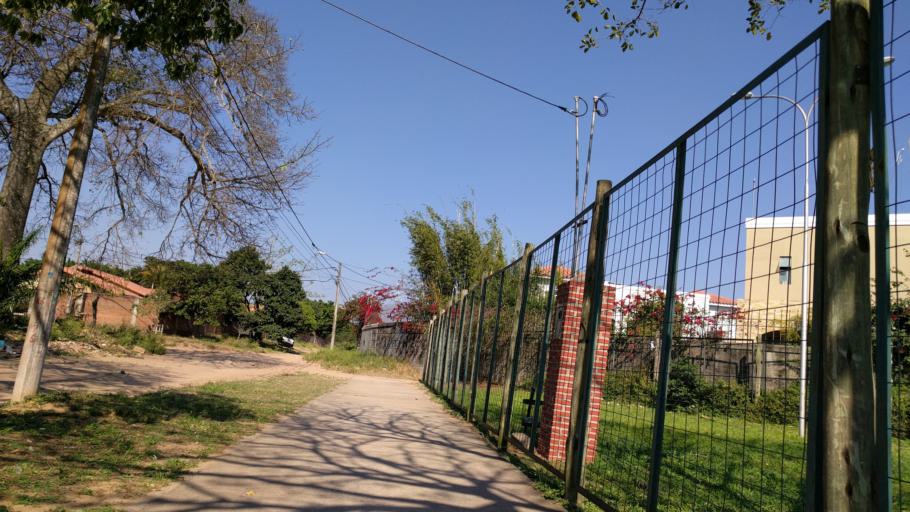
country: BO
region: Santa Cruz
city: Santa Cruz de la Sierra
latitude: -17.8127
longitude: -63.2269
